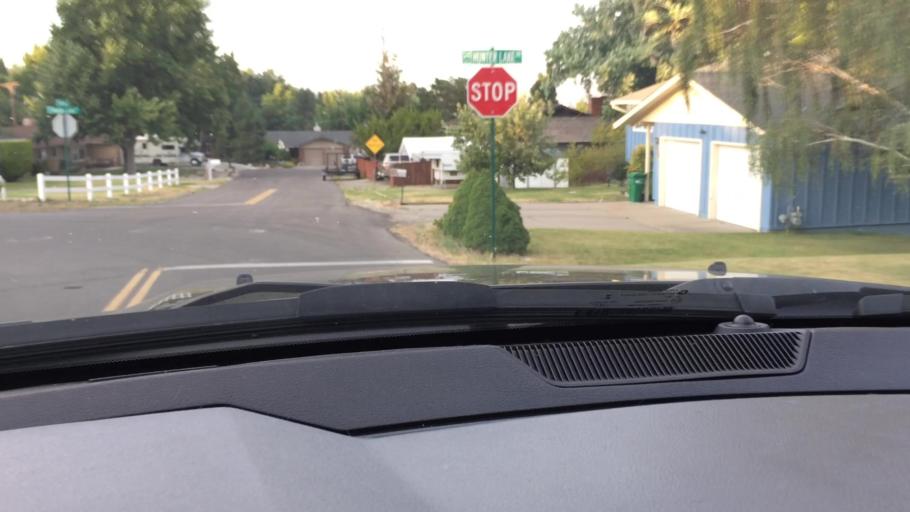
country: US
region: Nevada
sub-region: Washoe County
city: Reno
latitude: 39.4965
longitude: -119.8370
